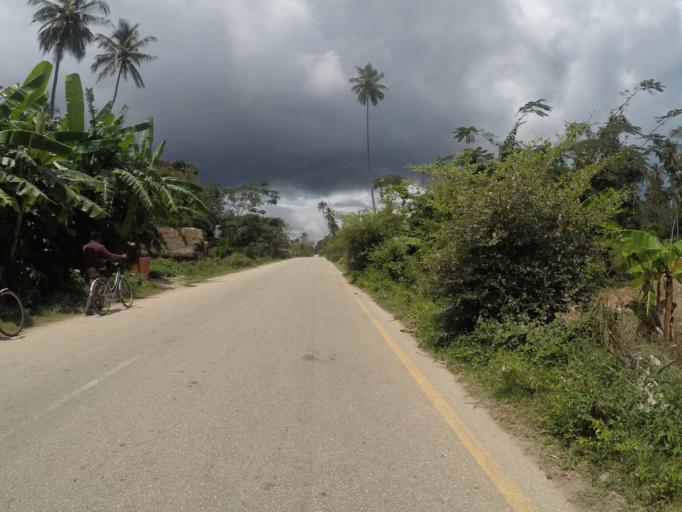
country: TZ
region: Zanzibar North
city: Mkokotoni
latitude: -5.9931
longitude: 39.1869
